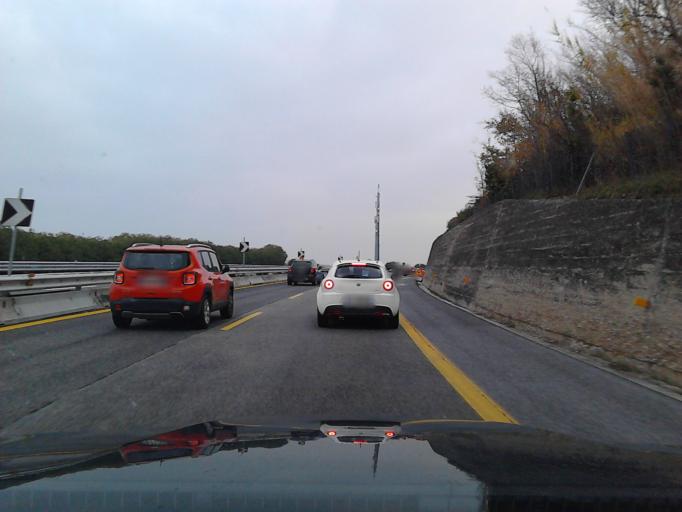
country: IT
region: Abruzzo
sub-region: Provincia di Teramo
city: Tortoreto Lido
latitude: 42.7949
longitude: 13.9330
